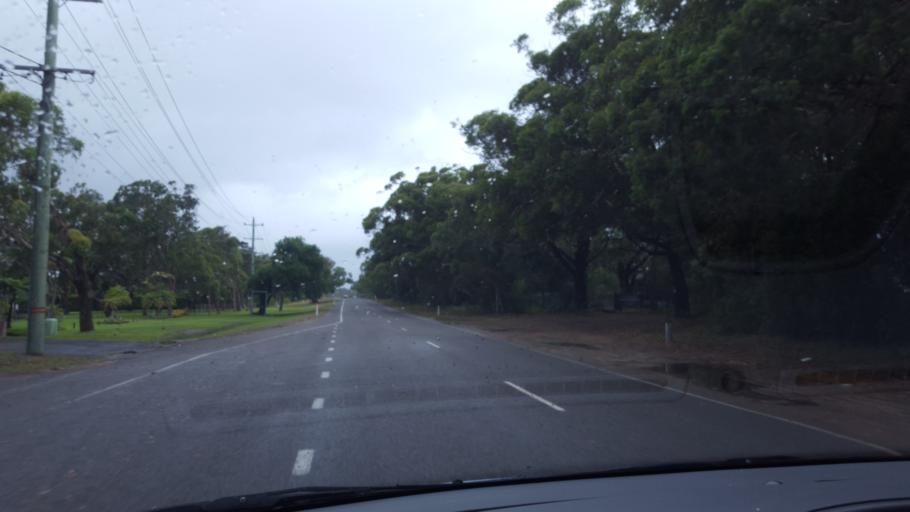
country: AU
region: New South Wales
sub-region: Port Stephens Shire
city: Anna Bay
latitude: -32.7719
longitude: 152.0763
